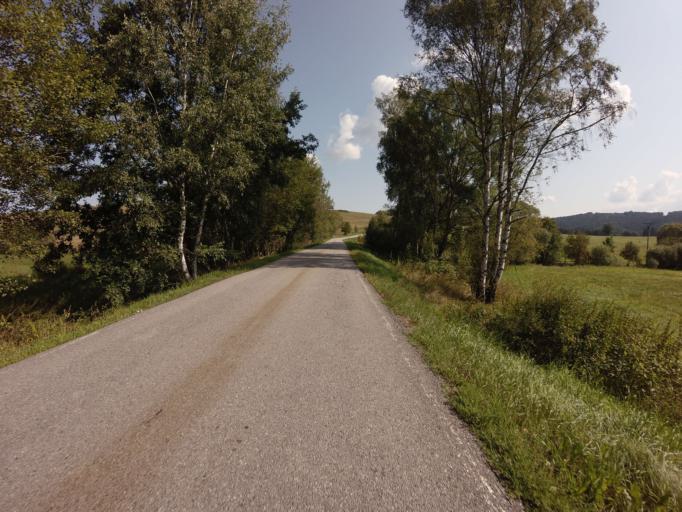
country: CZ
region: Jihocesky
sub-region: Okres Cesky Krumlov
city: Vyssi Brod
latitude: 48.6399
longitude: 14.3513
